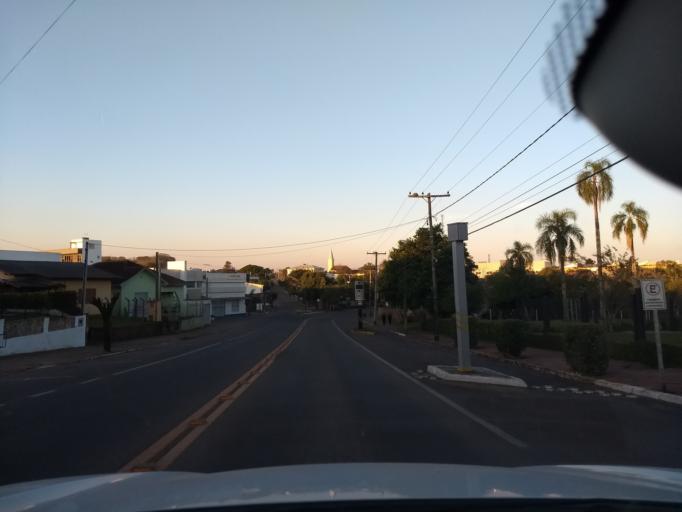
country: BR
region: Rio Grande do Sul
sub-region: Santa Cruz Do Sul
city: Santa Cruz do Sul
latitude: -29.7175
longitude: -52.5095
